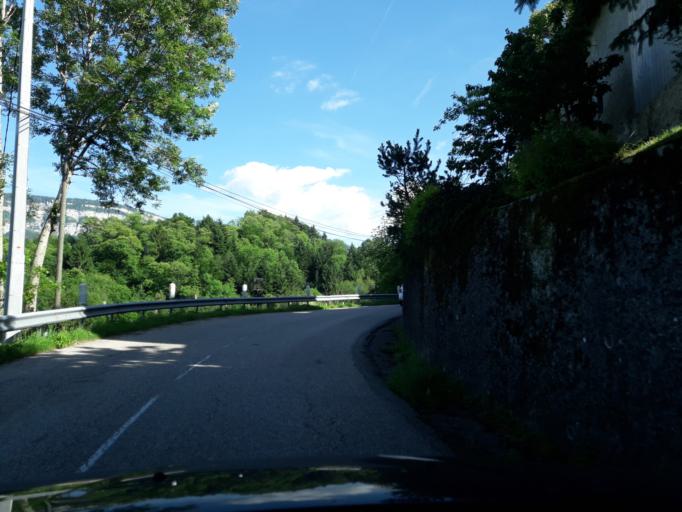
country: FR
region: Rhone-Alpes
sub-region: Departement de la Savoie
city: La Bridoire
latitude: 45.5398
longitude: 5.7611
